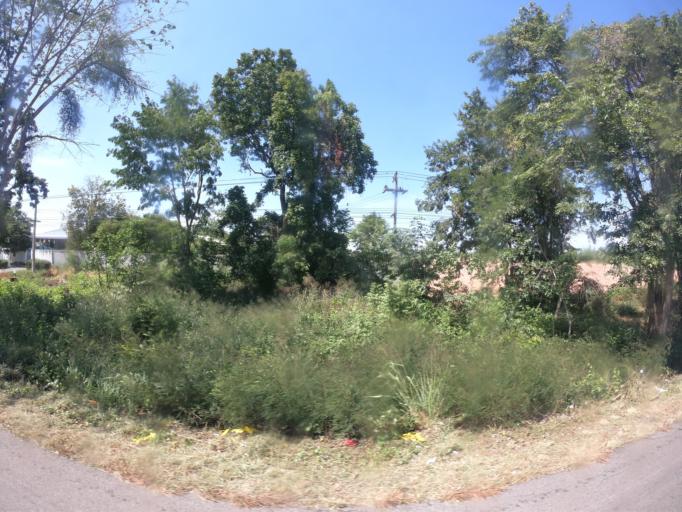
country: TH
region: Khon Kaen
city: Non Sila
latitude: 15.9029
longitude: 102.6530
